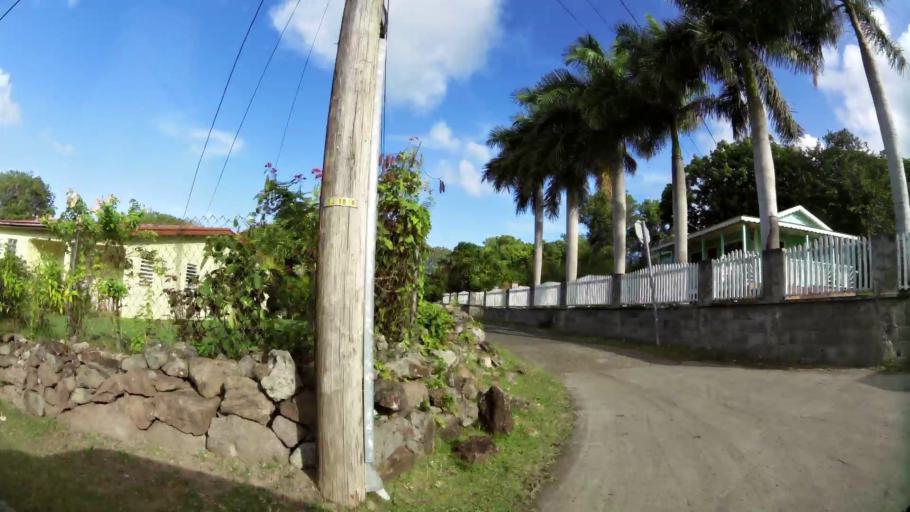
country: KN
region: Saint Paul Charlestown
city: Charlestown
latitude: 17.1281
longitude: -62.6054
